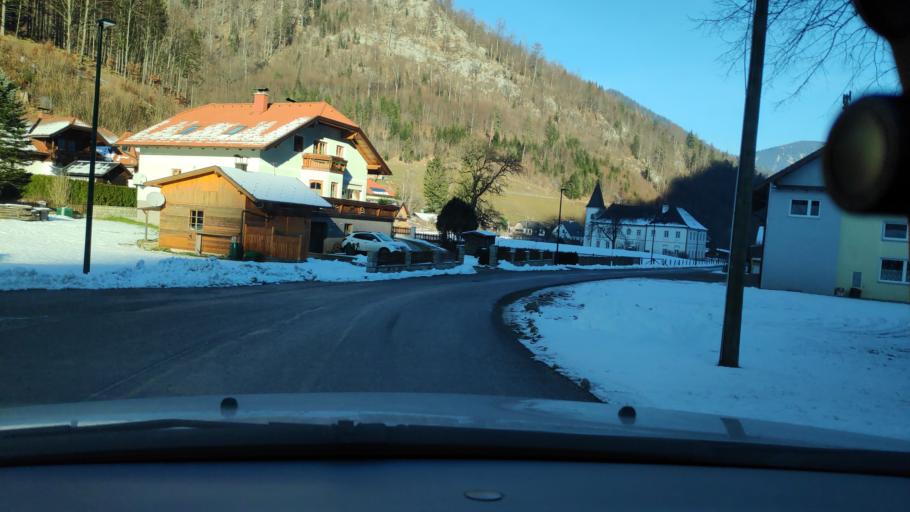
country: AT
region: Lower Austria
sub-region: Politischer Bezirk Neunkirchen
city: Schwarzau im Gebirge
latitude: 47.7622
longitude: 15.6949
